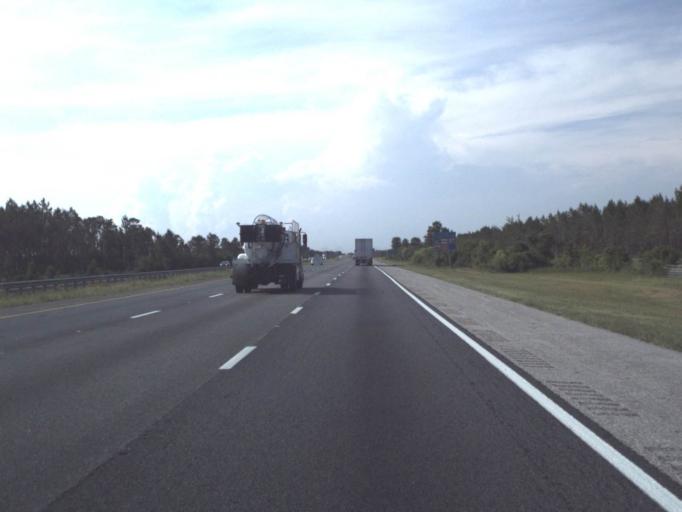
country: US
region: Florida
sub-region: Saint Johns County
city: Saint Augustine Shores
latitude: 29.7342
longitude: -81.3409
